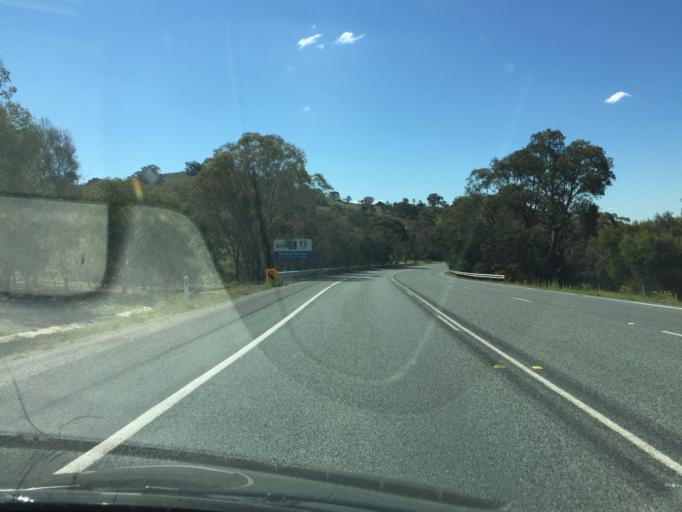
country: AU
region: Australian Capital Territory
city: Macarthur
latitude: -35.4575
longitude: 149.1311
